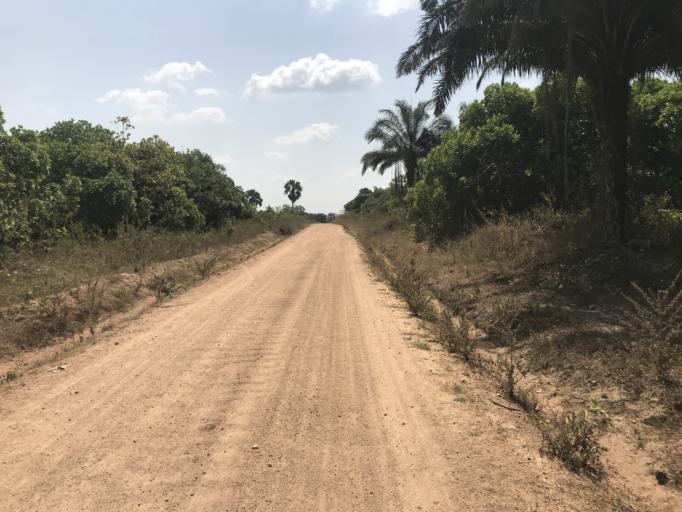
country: NG
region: Osun
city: Ifon
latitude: 7.9380
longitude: 4.4858
